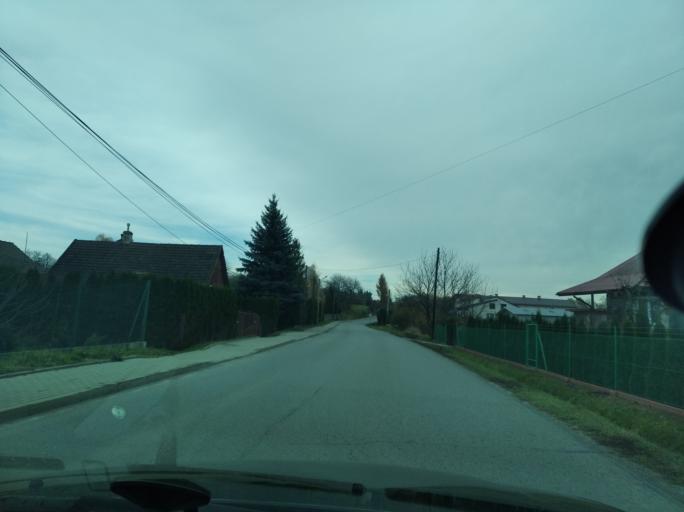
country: PL
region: Subcarpathian Voivodeship
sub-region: Powiat lancucki
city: Albigowa
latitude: 50.0337
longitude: 22.2314
